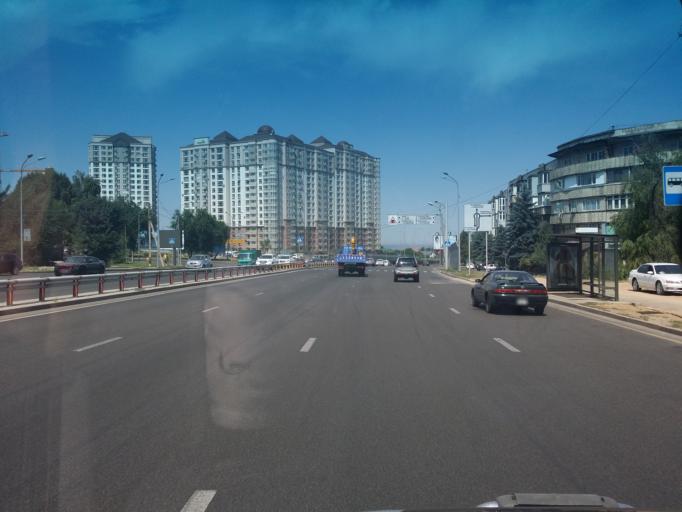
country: KZ
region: Almaty Qalasy
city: Almaty
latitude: 43.1969
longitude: 76.8726
